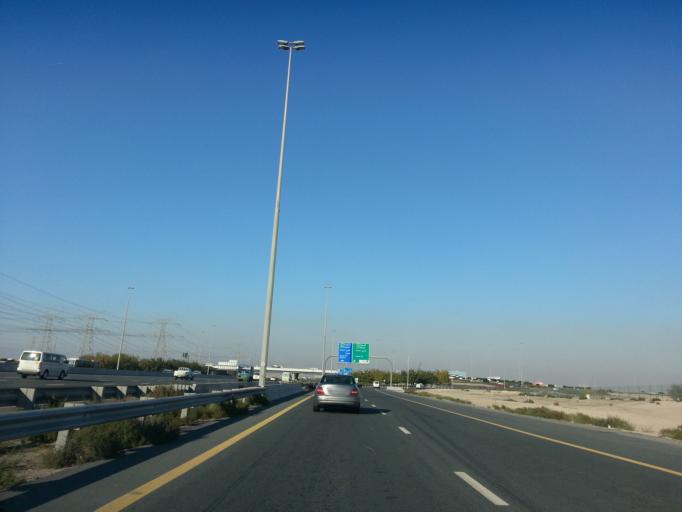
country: AE
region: Dubai
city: Dubai
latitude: 25.0736
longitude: 55.2081
